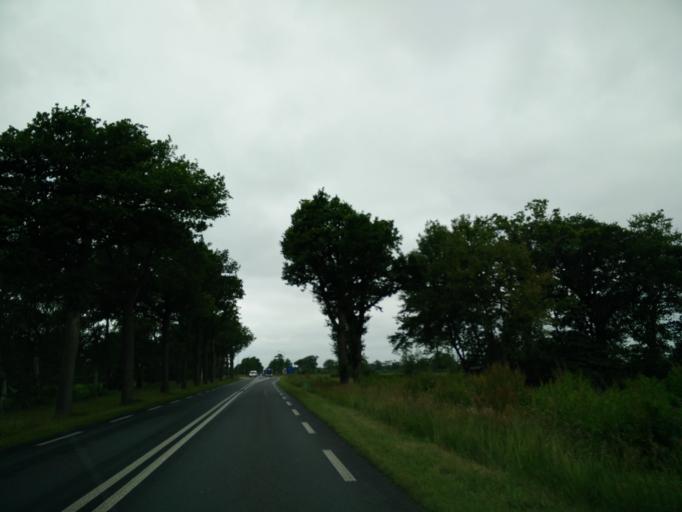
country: NL
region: Groningen
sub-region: Gemeente Leek
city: Leek
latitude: 53.1479
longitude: 6.4791
